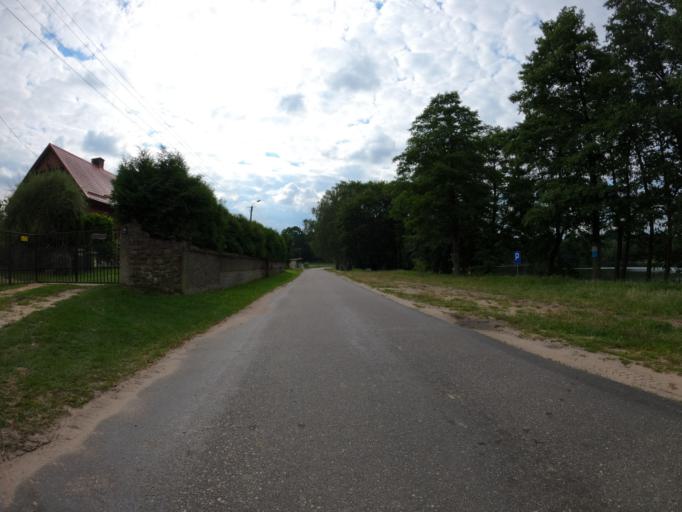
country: PL
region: West Pomeranian Voivodeship
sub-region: Powiat szczecinecki
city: Borne Sulinowo
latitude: 53.6289
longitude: 16.5610
